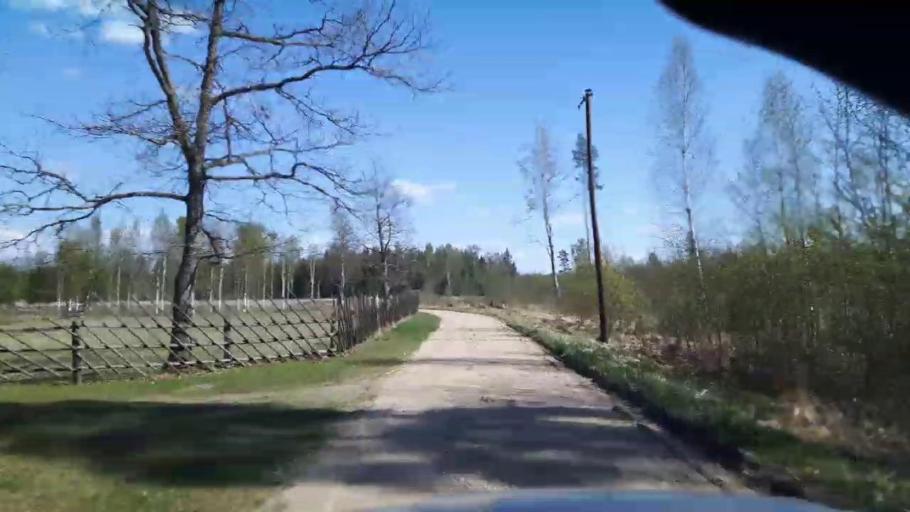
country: EE
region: Paernumaa
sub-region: Tootsi vald
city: Tootsi
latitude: 58.5414
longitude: 24.8108
